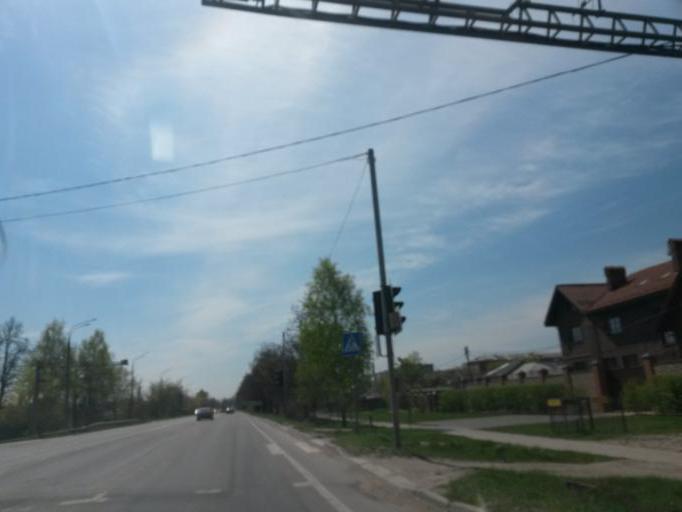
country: RU
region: Moskovskaya
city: Klimovsk
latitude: 55.3922
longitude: 37.5442
